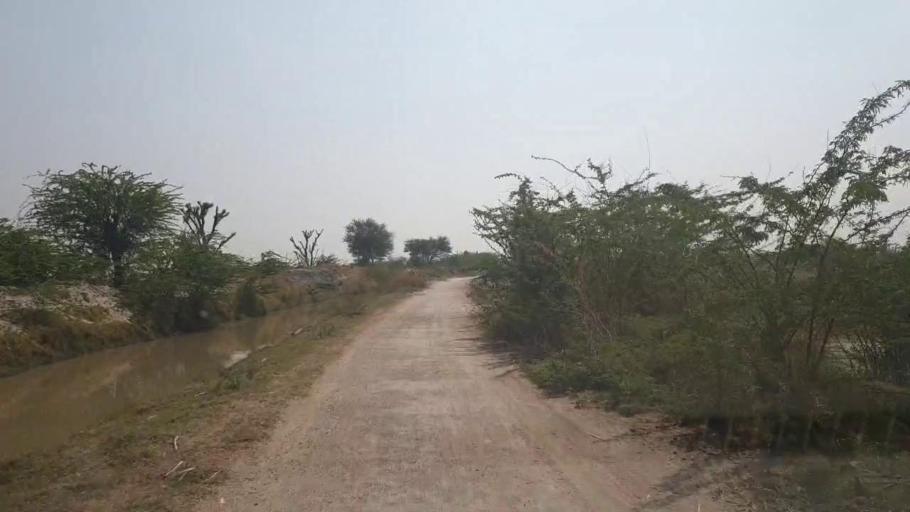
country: PK
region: Sindh
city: Dhoro Naro
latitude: 25.5158
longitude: 69.5410
